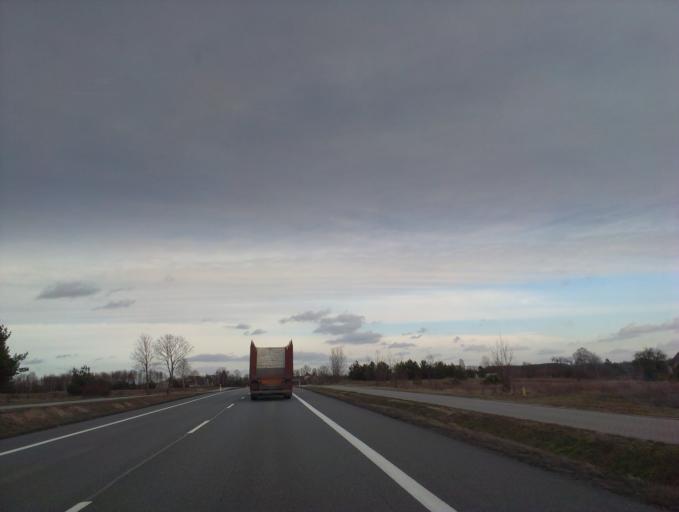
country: PL
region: Kujawsko-Pomorskie
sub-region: Powiat lipnowski
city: Skepe
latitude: 52.8897
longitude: 19.4119
